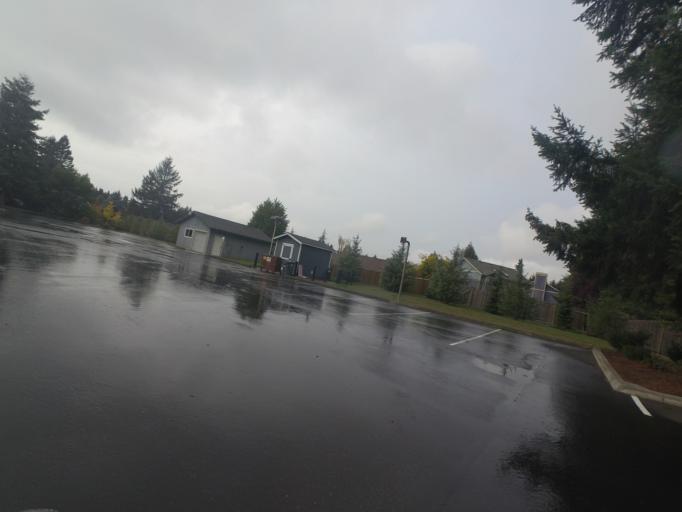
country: US
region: Washington
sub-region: Pierce County
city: University Place
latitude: 47.2213
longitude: -122.5426
